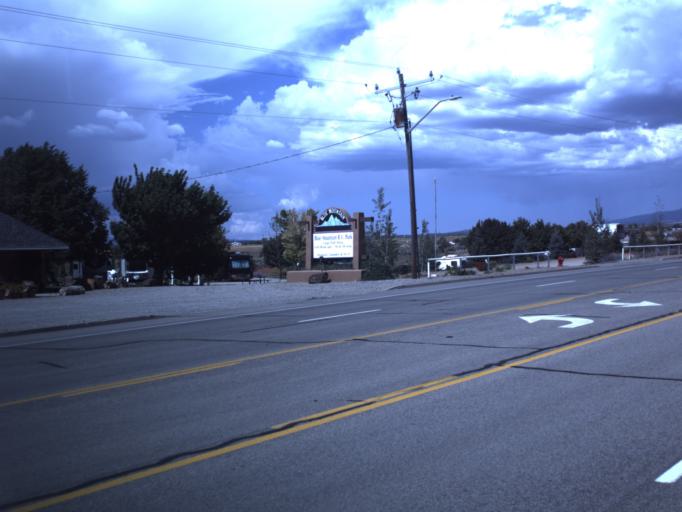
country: US
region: Utah
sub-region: San Juan County
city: Blanding
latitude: 37.5973
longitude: -109.4785
